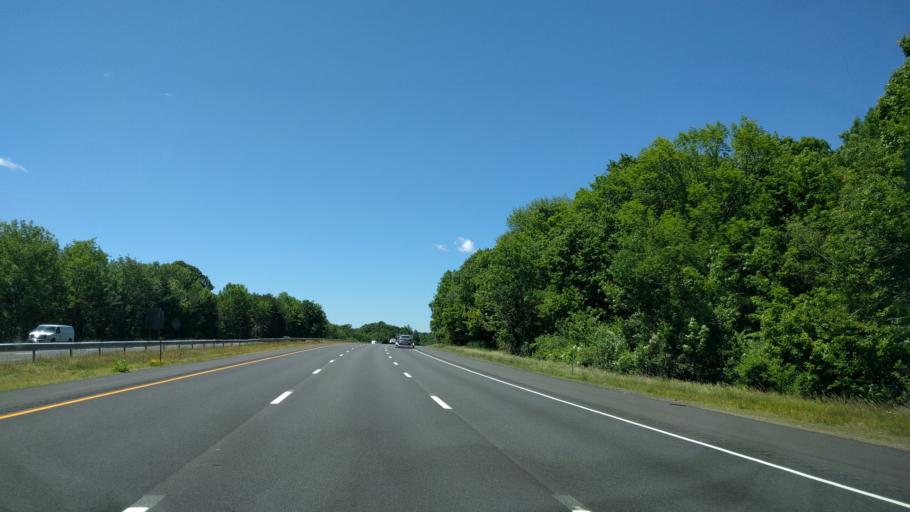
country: US
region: Connecticut
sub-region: Tolland County
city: Stafford
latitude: 41.9488
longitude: -72.2046
